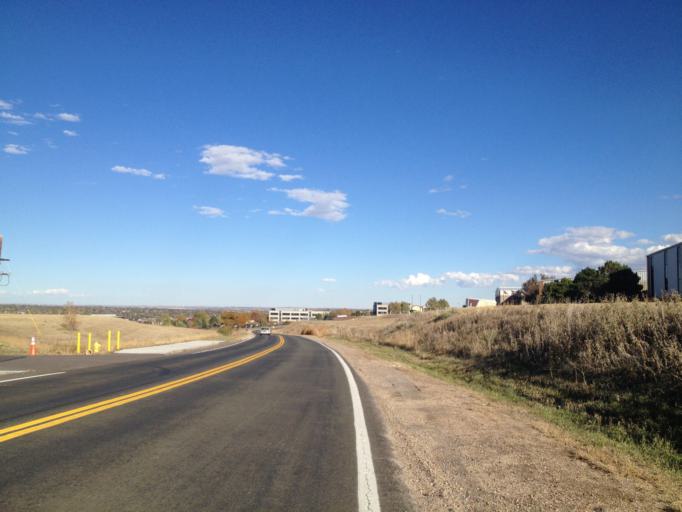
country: US
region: Colorado
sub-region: Broomfield County
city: Broomfield
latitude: 39.9141
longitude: -105.1151
